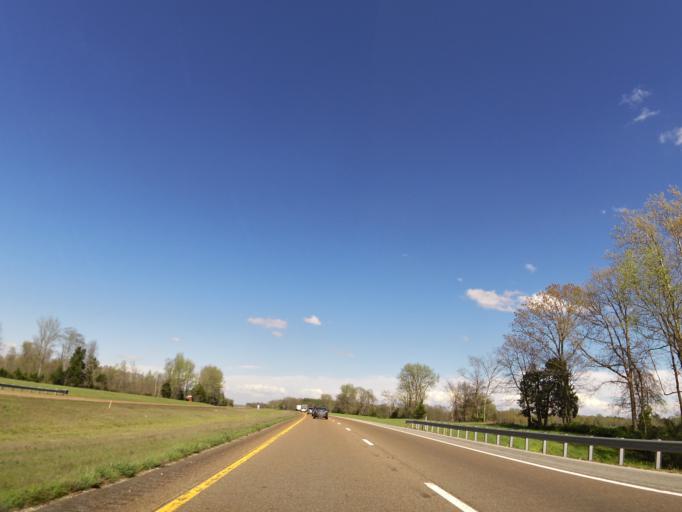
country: US
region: Tennessee
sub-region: Gibson County
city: Medina
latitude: 35.7281
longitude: -88.6015
